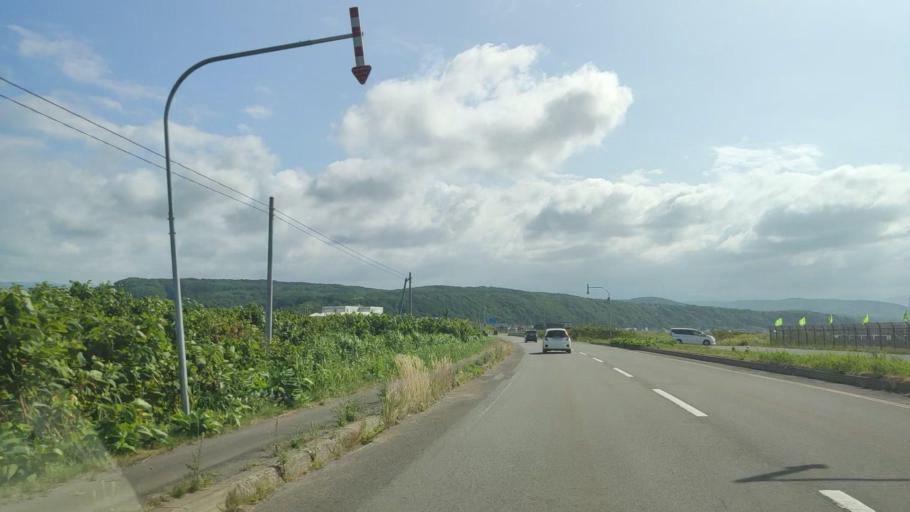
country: JP
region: Hokkaido
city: Rumoi
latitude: 43.8777
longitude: 141.5854
